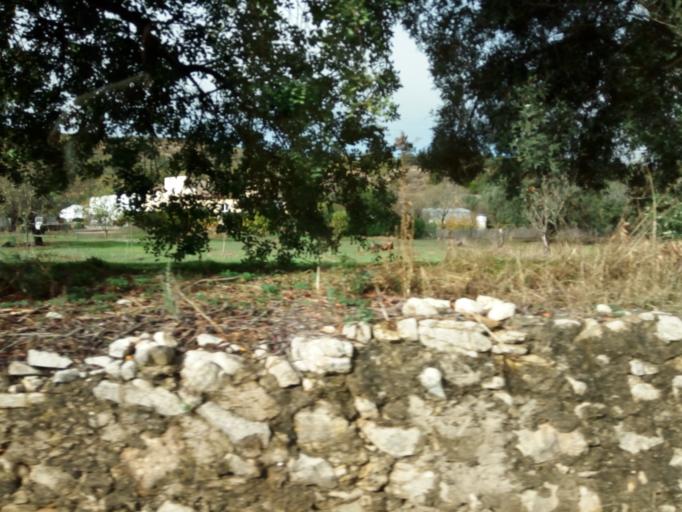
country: PT
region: Faro
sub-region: Faro
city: Santa Barbara de Nexe
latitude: 37.1182
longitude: -7.9583
